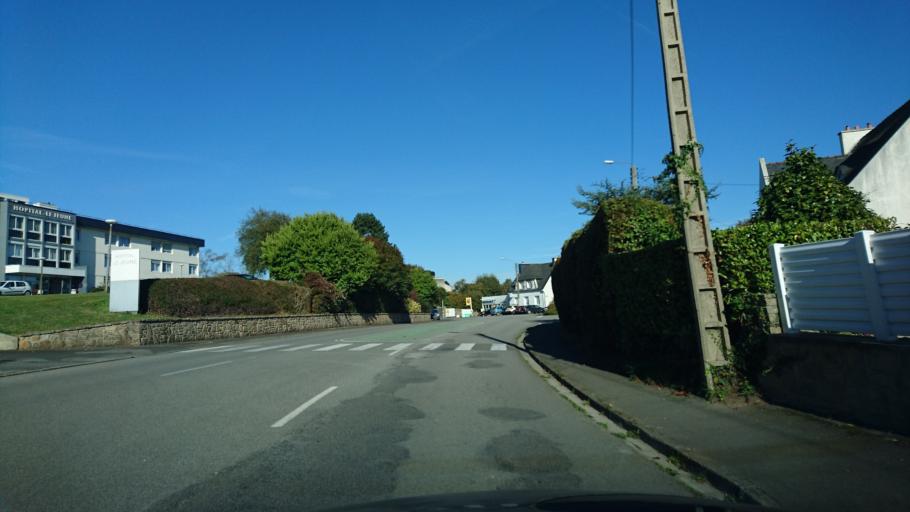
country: FR
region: Brittany
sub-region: Departement du Finistere
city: Saint-Renan
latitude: 48.4290
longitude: -4.6187
